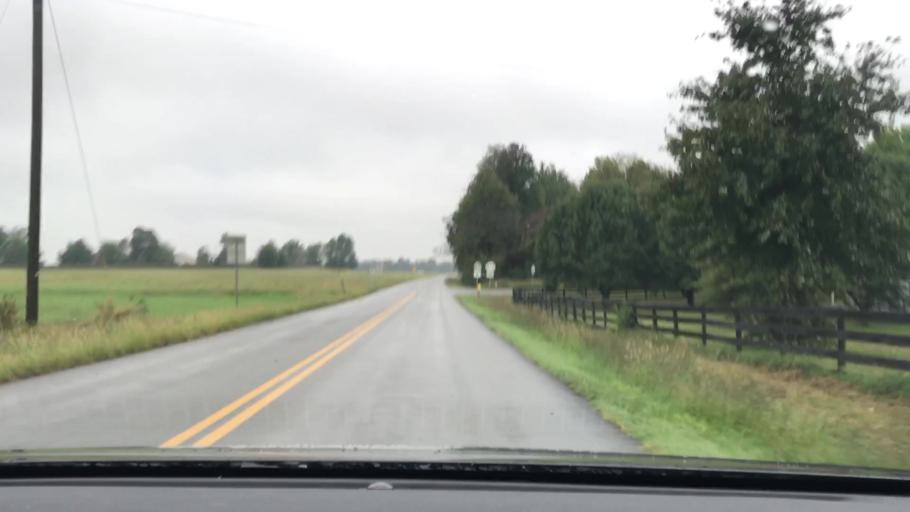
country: US
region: Kentucky
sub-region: Hopkins County
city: Madisonville
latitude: 37.3709
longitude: -87.3549
